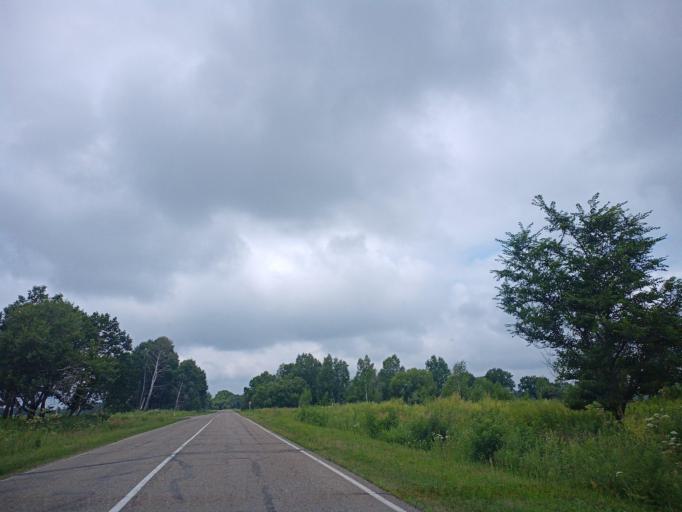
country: RU
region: Primorskiy
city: Dal'nerechensk
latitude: 45.9482
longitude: 133.9130
